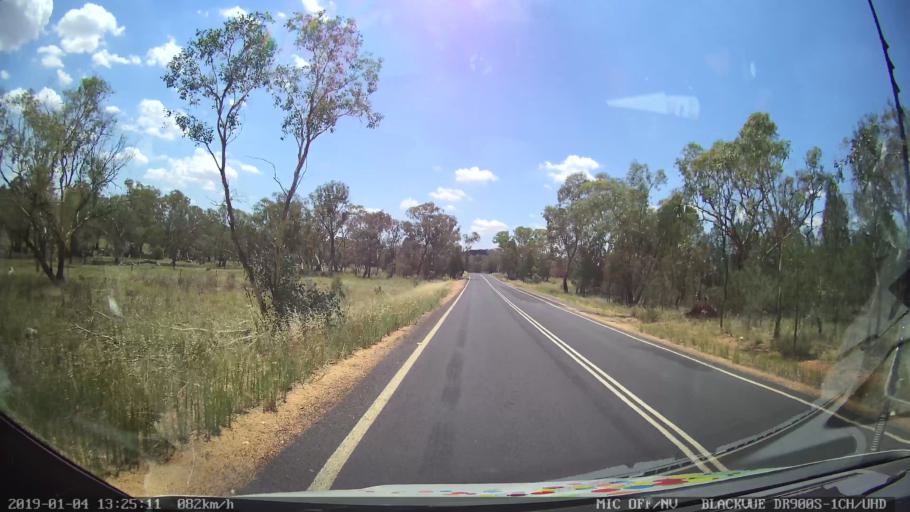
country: AU
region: New South Wales
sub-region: Parkes
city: Peak Hill
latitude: -32.6962
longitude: 148.5550
